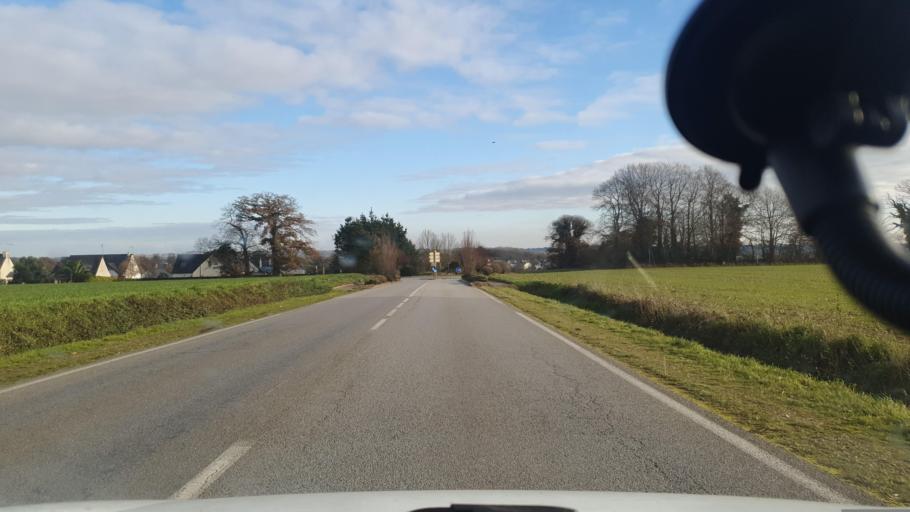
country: FR
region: Brittany
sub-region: Departement du Finistere
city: Briec
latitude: 48.0982
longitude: -4.0107
